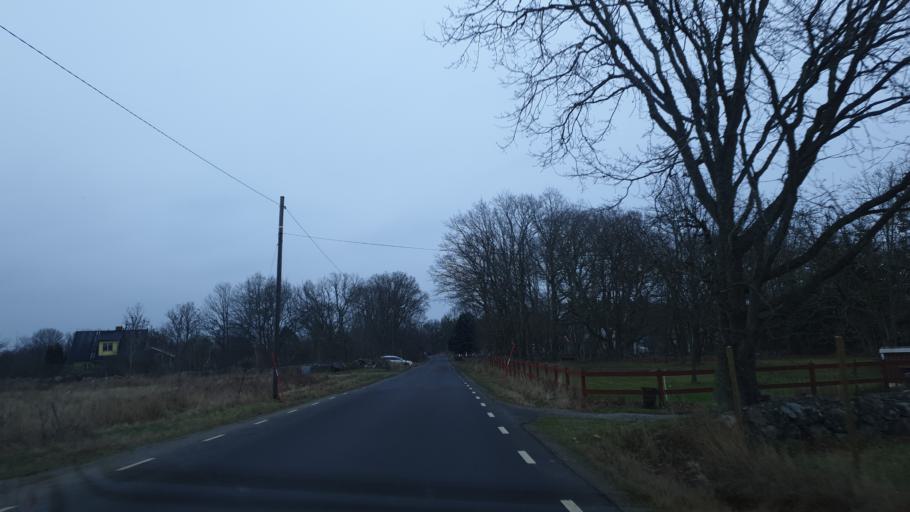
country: SE
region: Blekinge
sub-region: Karlskrona Kommun
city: Sturko
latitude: 56.1117
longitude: 15.6505
